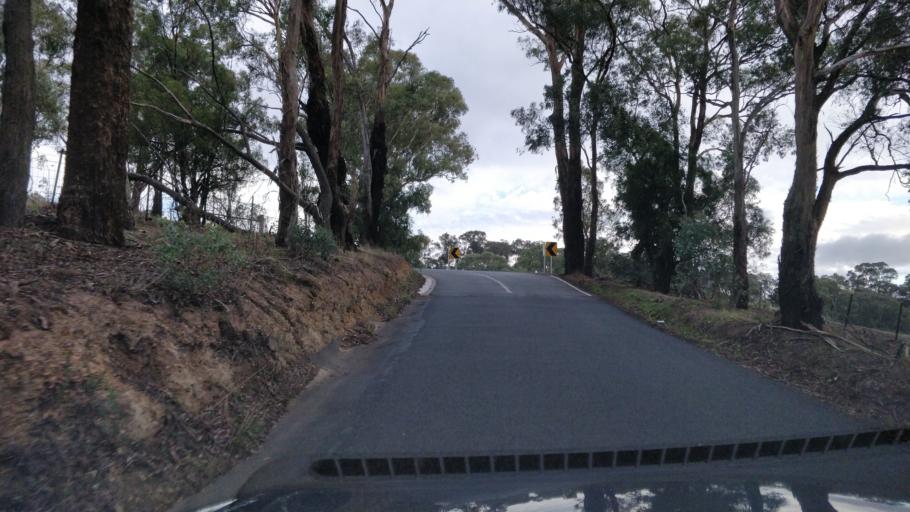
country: AU
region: Victoria
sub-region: Nillumbik
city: Research
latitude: -37.6869
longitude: 145.1766
